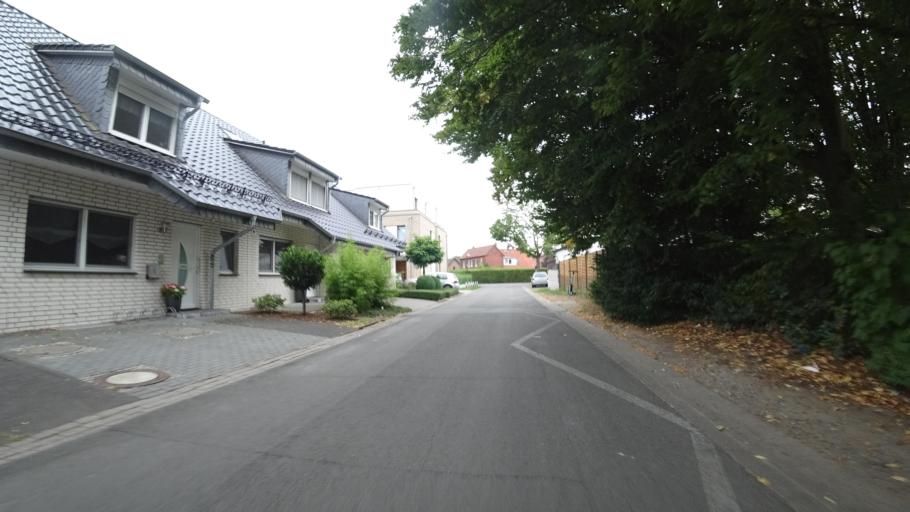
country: DE
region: North Rhine-Westphalia
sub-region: Regierungsbezirk Detmold
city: Guetersloh
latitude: 51.9151
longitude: 8.4137
